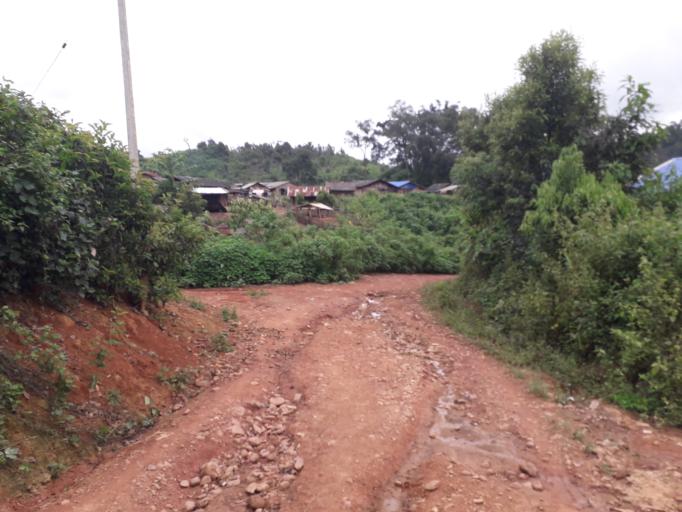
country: CN
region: Yunnan
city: Menglie
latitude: 22.2061
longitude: 101.6654
